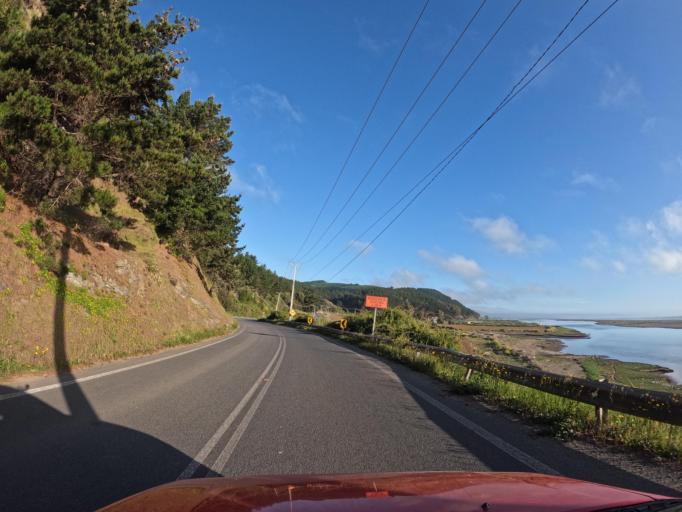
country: CL
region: Maule
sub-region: Provincia de Talca
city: Constitucion
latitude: -34.9824
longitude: -72.1809
